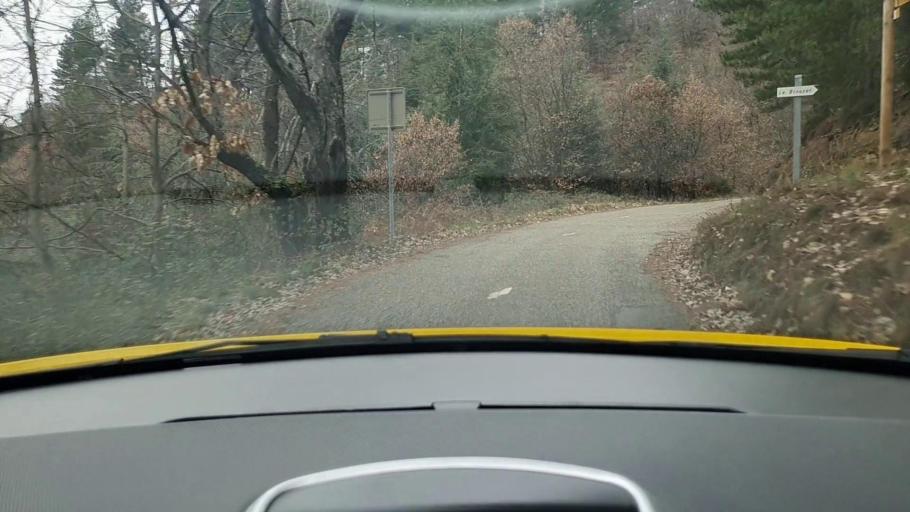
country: FR
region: Languedoc-Roussillon
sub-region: Departement du Gard
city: Besseges
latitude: 44.3560
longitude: 4.0211
